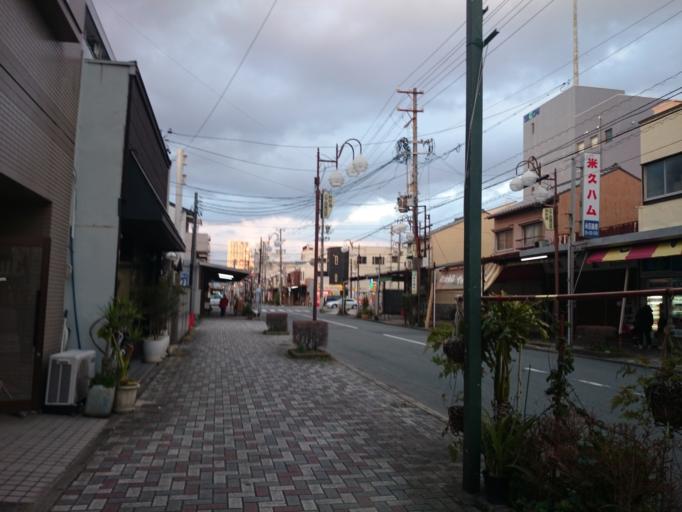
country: JP
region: Shizuoka
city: Shizuoka-shi
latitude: 34.9670
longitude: 138.3766
